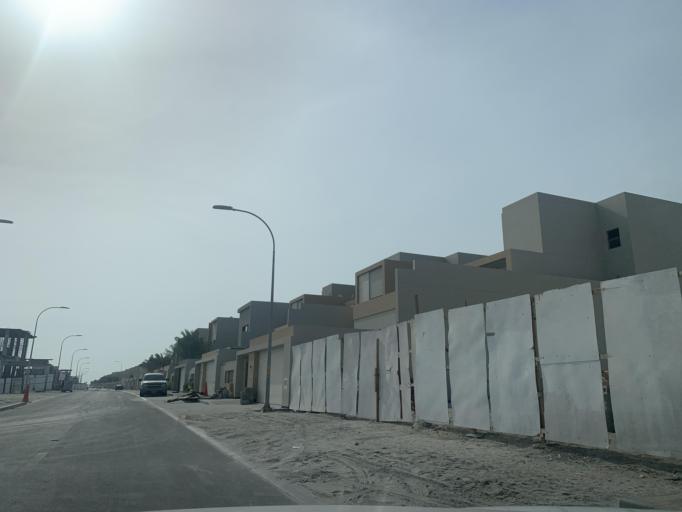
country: BH
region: Muharraq
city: Al Muharraq
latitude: 26.3230
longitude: 50.6310
